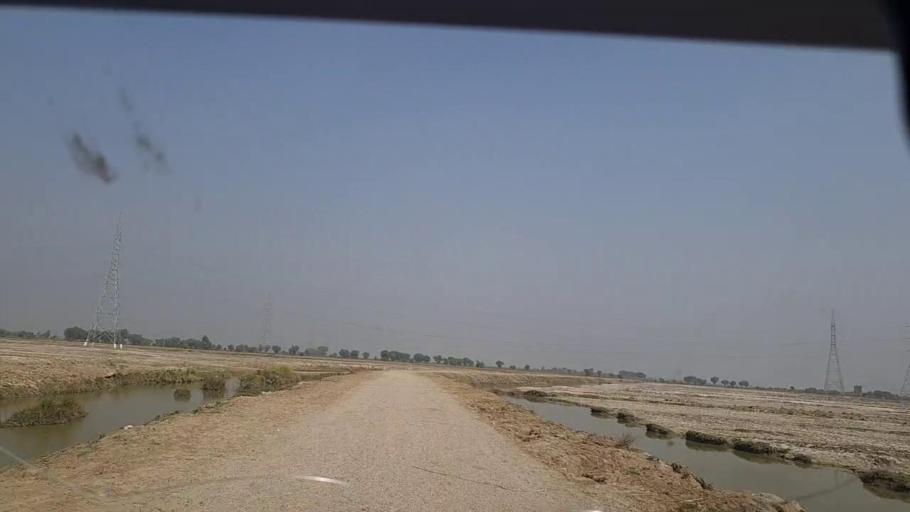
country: PK
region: Sindh
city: Shikarpur
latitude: 28.0342
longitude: 68.6308
